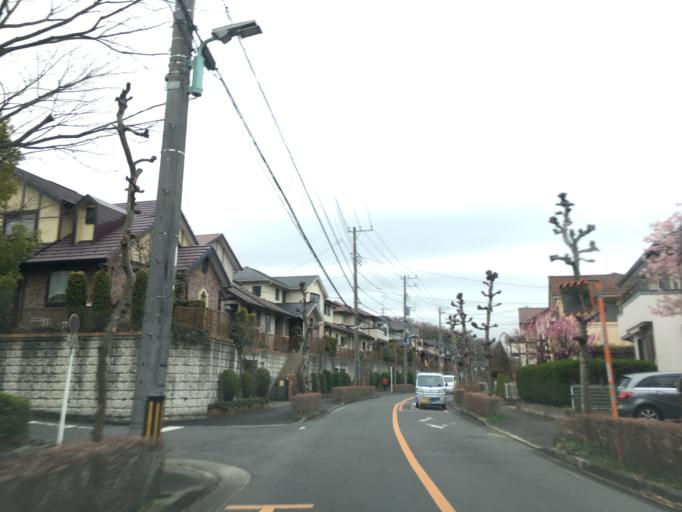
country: JP
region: Tokyo
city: Higashimurayama-shi
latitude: 35.7715
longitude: 139.4548
